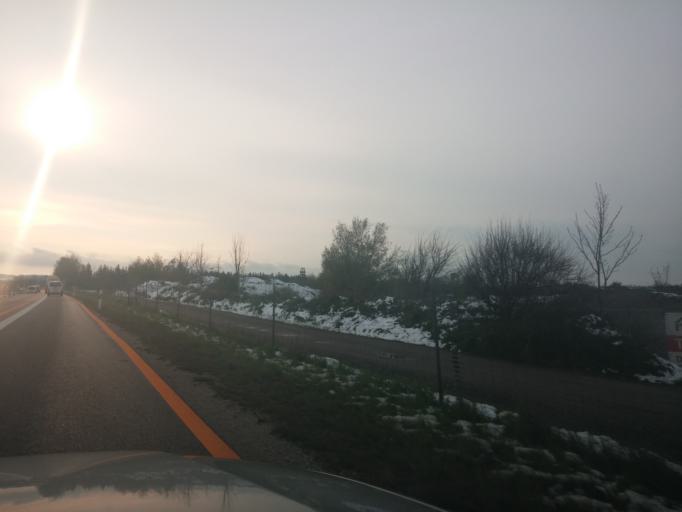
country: DE
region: Bavaria
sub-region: Swabia
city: Turkheim
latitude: 48.0408
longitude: 10.6294
